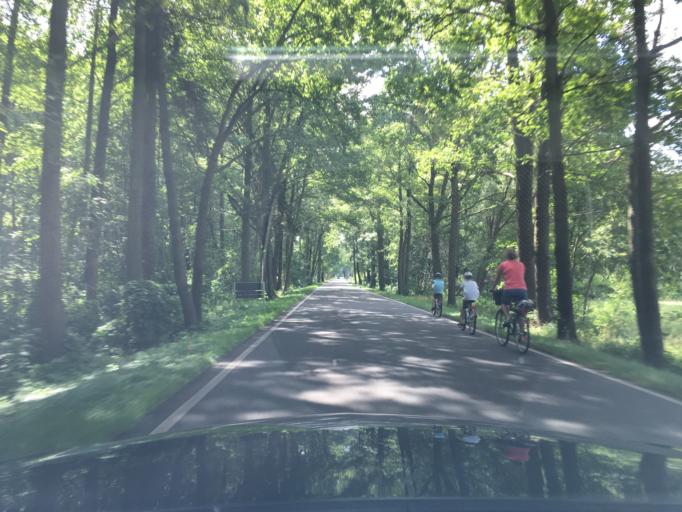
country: DE
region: Brandenburg
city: Burg
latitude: 51.8373
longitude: 14.1066
